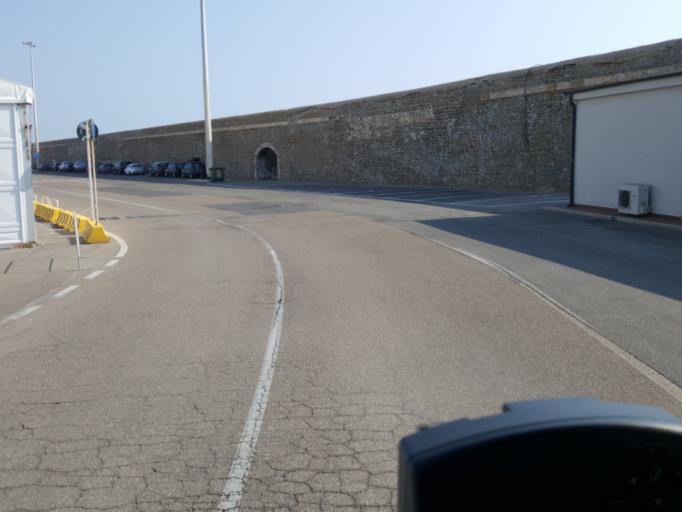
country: IT
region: Latium
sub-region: Citta metropolitana di Roma Capitale
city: Civitavecchia
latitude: 42.0906
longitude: 11.7854
